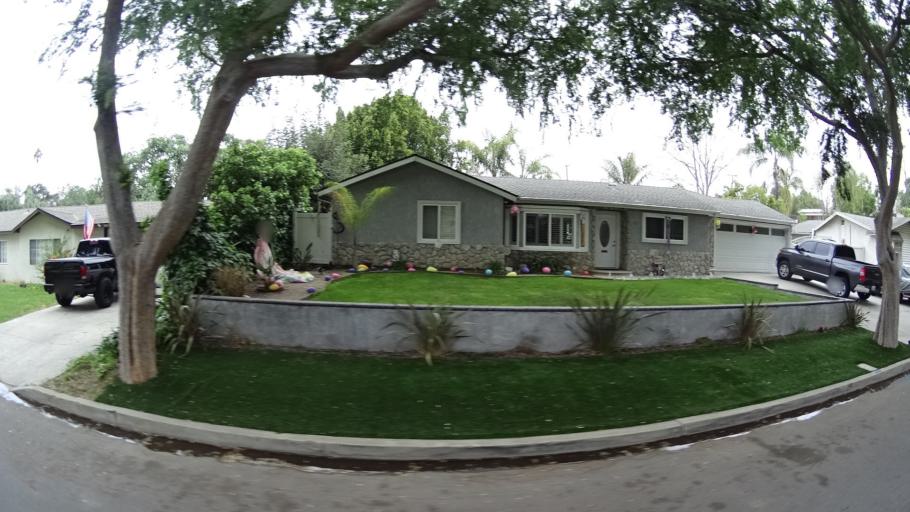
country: US
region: California
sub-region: Ventura County
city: Thousand Oaks
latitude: 34.2093
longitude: -118.8579
